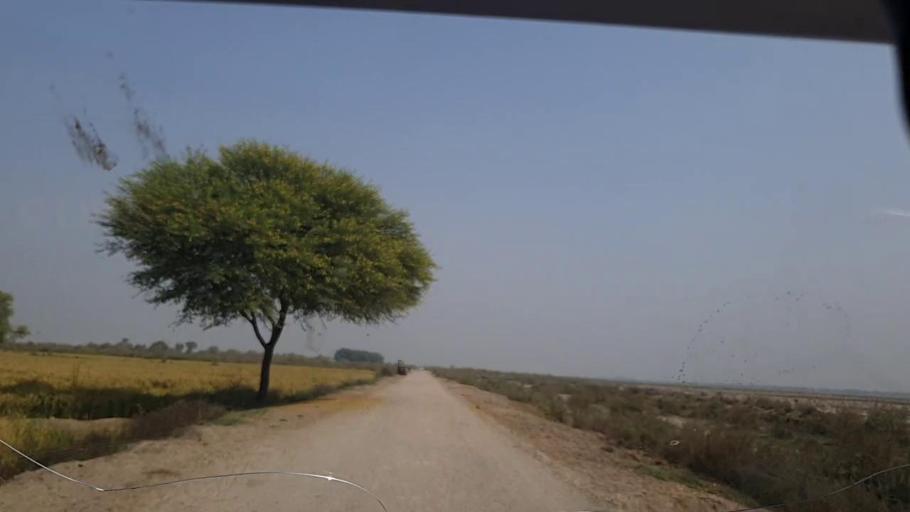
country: PK
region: Sindh
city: Shikarpur
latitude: 28.0370
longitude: 68.6378
